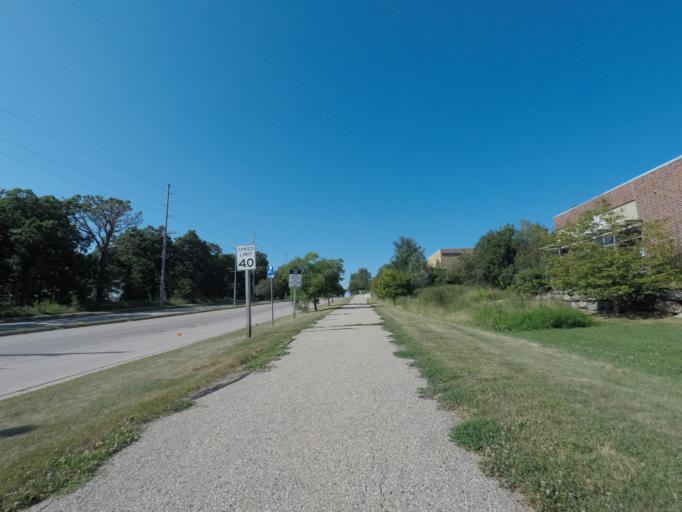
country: US
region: Wisconsin
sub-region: Dane County
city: Madison
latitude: 43.0191
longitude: -89.4198
